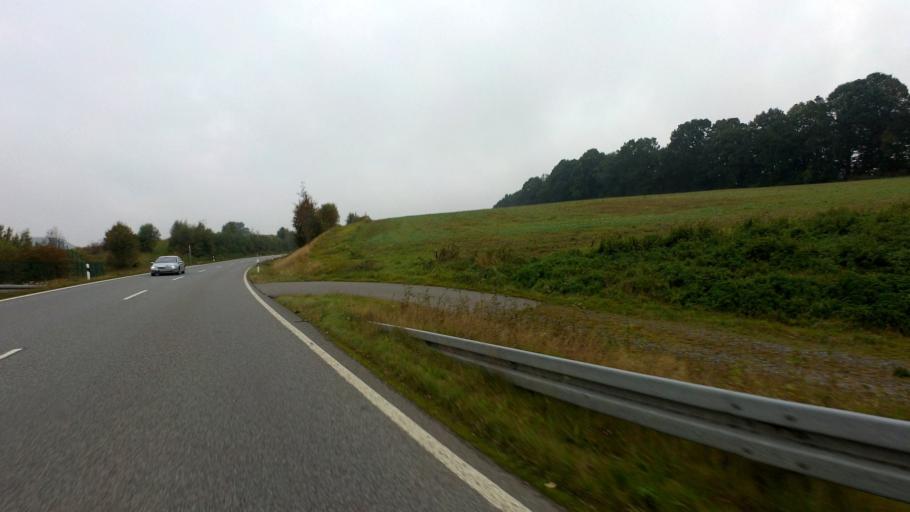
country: DE
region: Saxony
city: Neustadt in Sachsen
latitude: 51.0383
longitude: 14.2146
